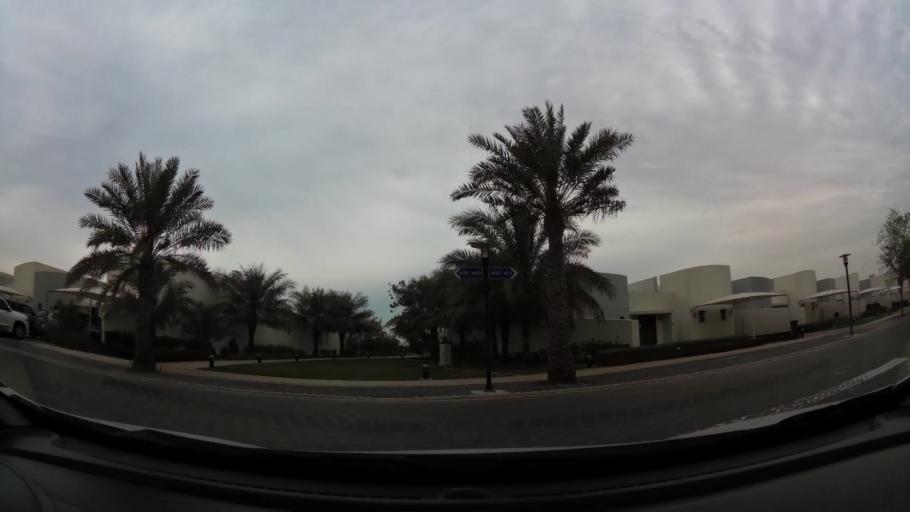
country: BH
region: Central Governorate
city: Dar Kulayb
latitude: 25.8340
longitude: 50.6134
